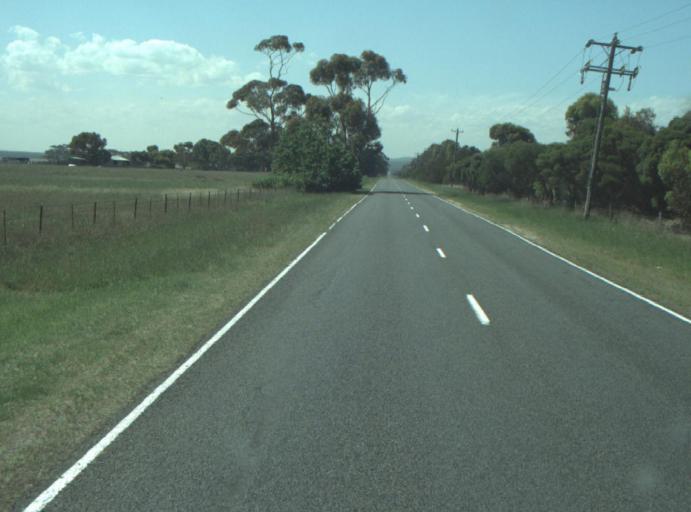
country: AU
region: Victoria
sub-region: Greater Geelong
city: Lara
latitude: -38.0052
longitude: 144.3995
